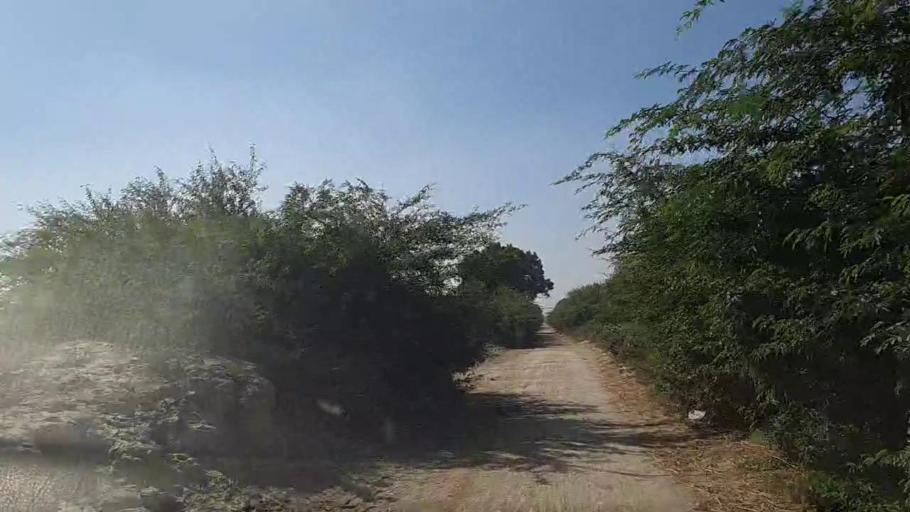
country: PK
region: Sindh
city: Daro Mehar
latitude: 24.8382
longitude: 68.1282
